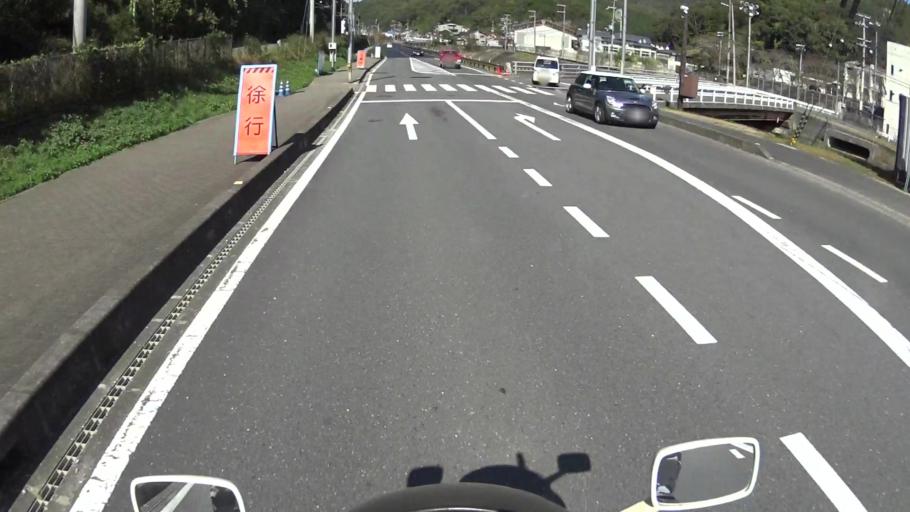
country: JP
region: Kyoto
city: Kameoka
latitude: 35.1581
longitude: 135.5062
